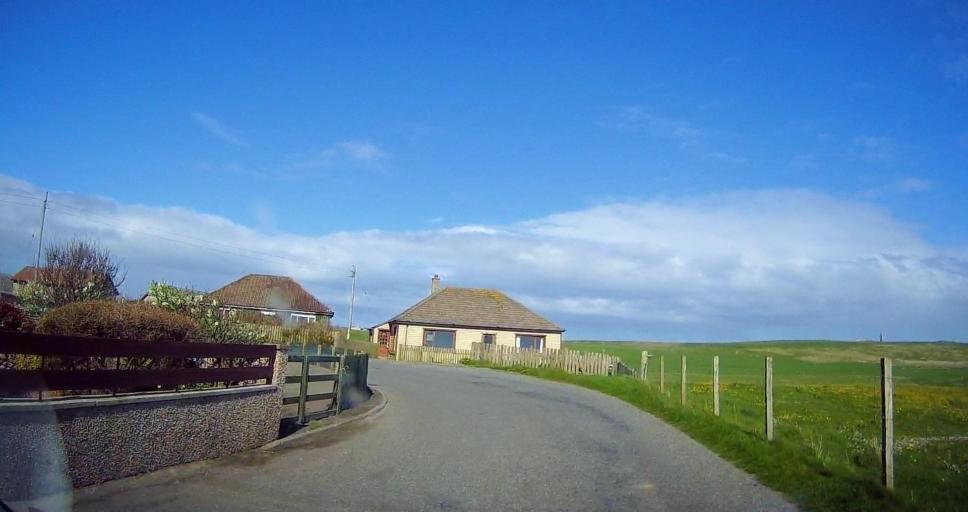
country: GB
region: Scotland
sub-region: Shetland Islands
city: Sandwick
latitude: 59.9124
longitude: -1.3243
